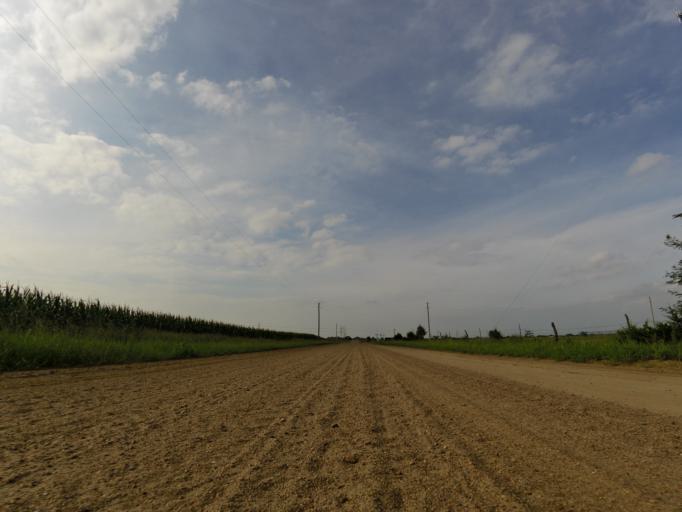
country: US
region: Kansas
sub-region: Reno County
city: South Hutchinson
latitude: 37.9747
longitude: -98.0687
